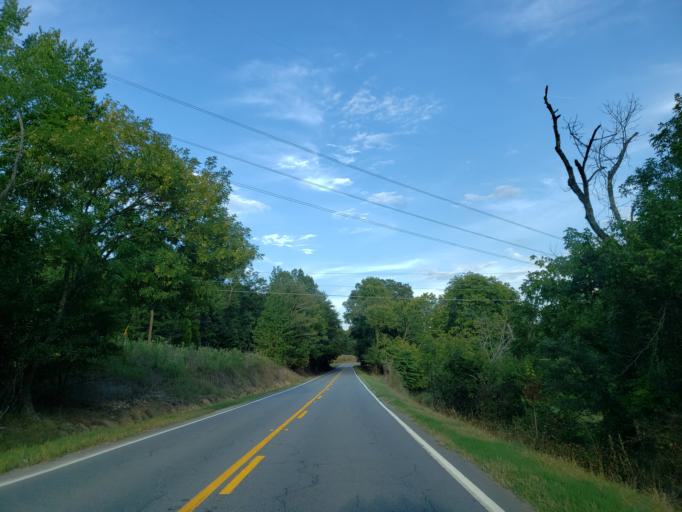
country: US
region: Georgia
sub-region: Bartow County
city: Euharlee
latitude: 34.2452
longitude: -84.9166
